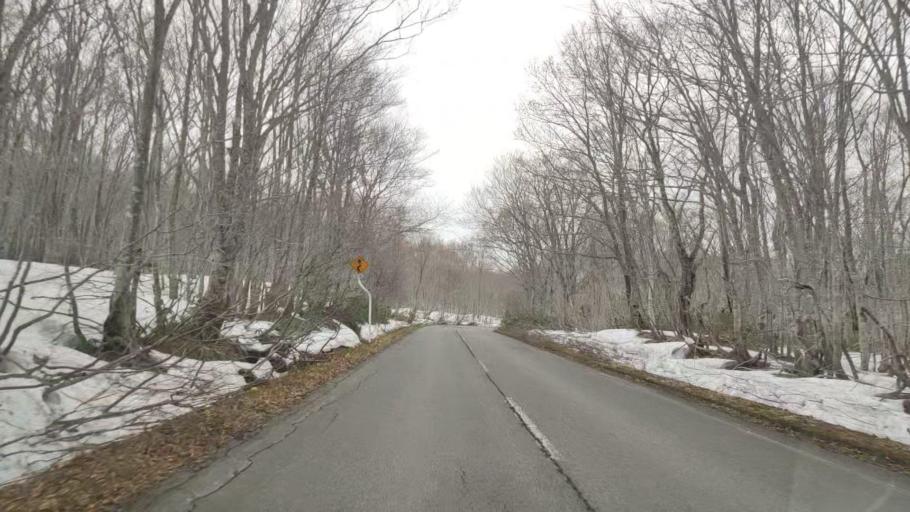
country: JP
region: Aomori
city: Aomori Shi
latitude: 40.6515
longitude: 140.9468
